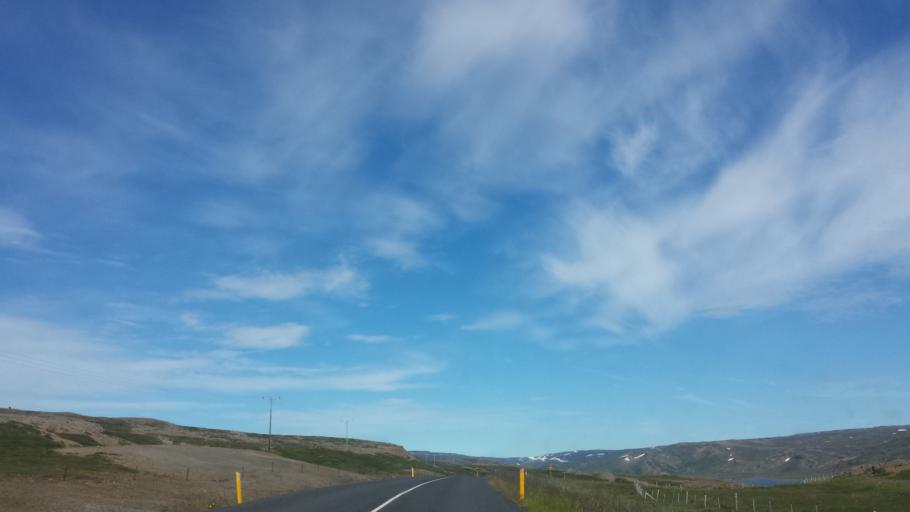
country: IS
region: West
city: Stykkisholmur
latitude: 65.7406
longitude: -21.7075
